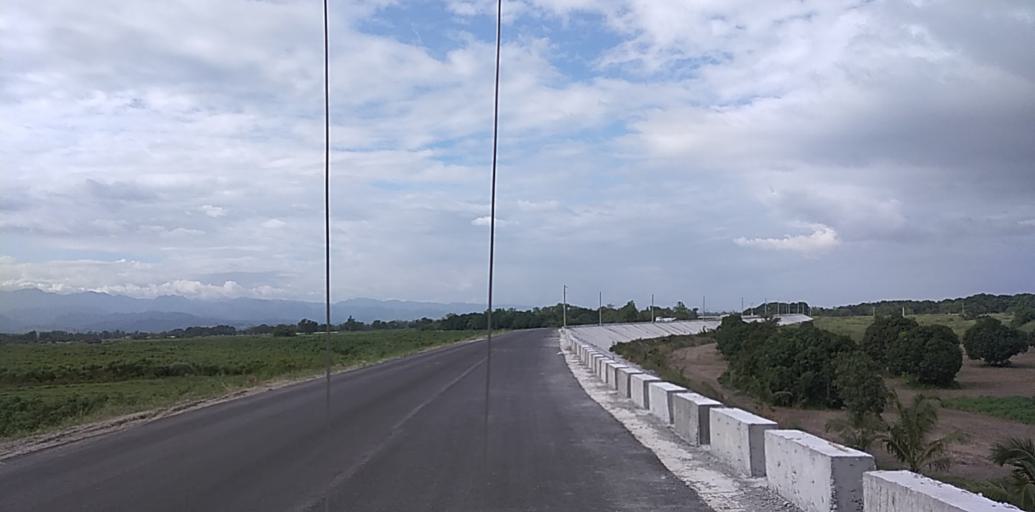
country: PH
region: Central Luzon
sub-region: Province of Pampanga
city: Pulung Santol
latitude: 15.0624
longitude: 120.5617
